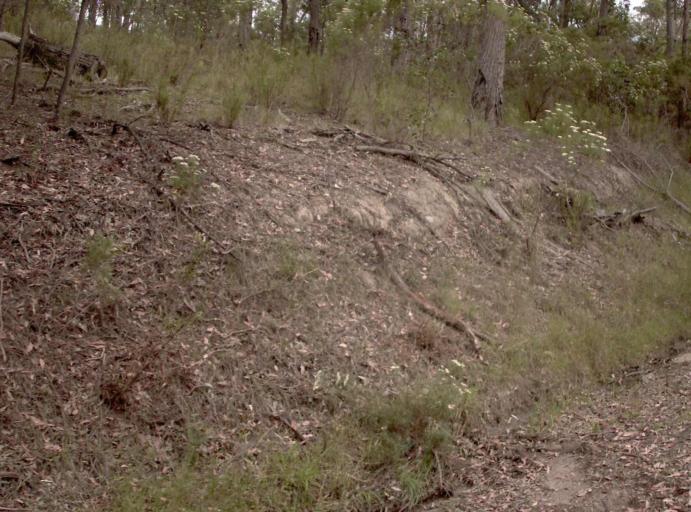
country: AU
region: Victoria
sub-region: East Gippsland
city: Bairnsdale
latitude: -37.7069
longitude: 147.5923
